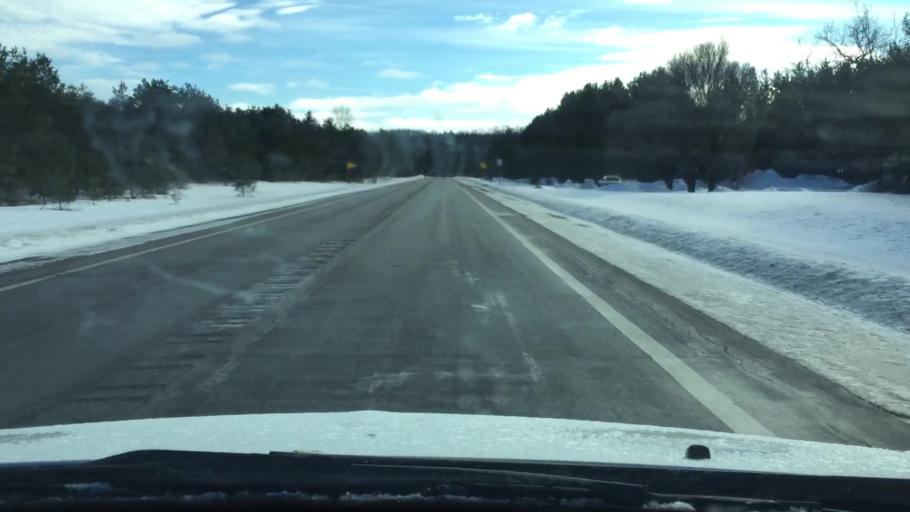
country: US
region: Michigan
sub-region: Antrim County
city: Mancelona
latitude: 44.9623
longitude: -85.0518
